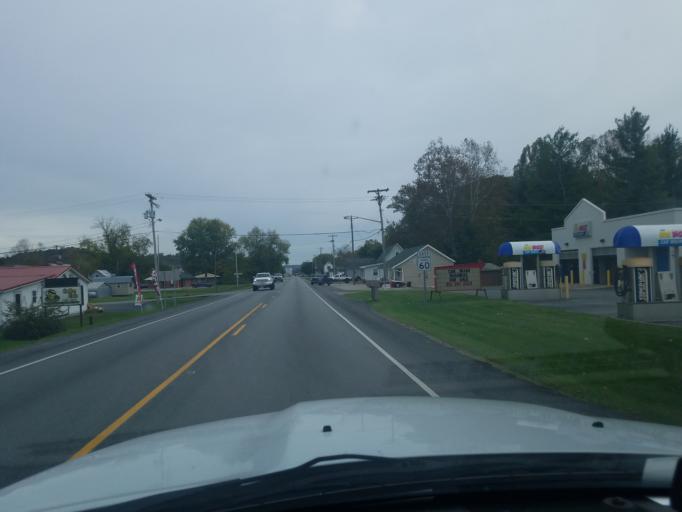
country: US
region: Indiana
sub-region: Washington County
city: New Pekin
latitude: 38.4668
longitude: -85.9470
